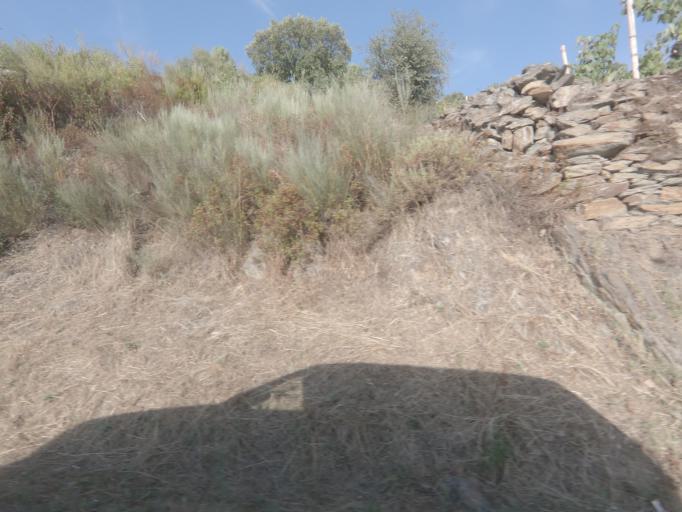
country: PT
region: Vila Real
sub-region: Sabrosa
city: Sabrosa
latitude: 41.2266
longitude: -7.5244
